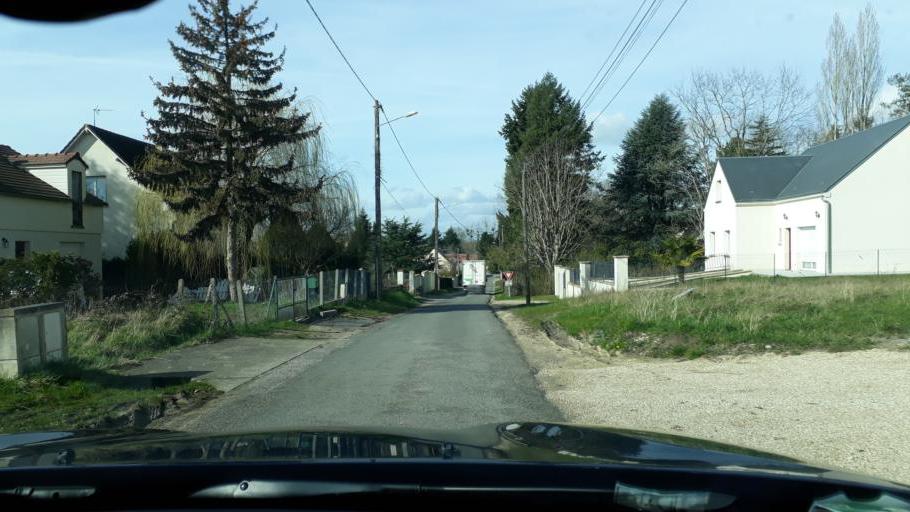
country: FR
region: Centre
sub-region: Departement du Loiret
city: Donnery
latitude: 47.9121
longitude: 2.1100
